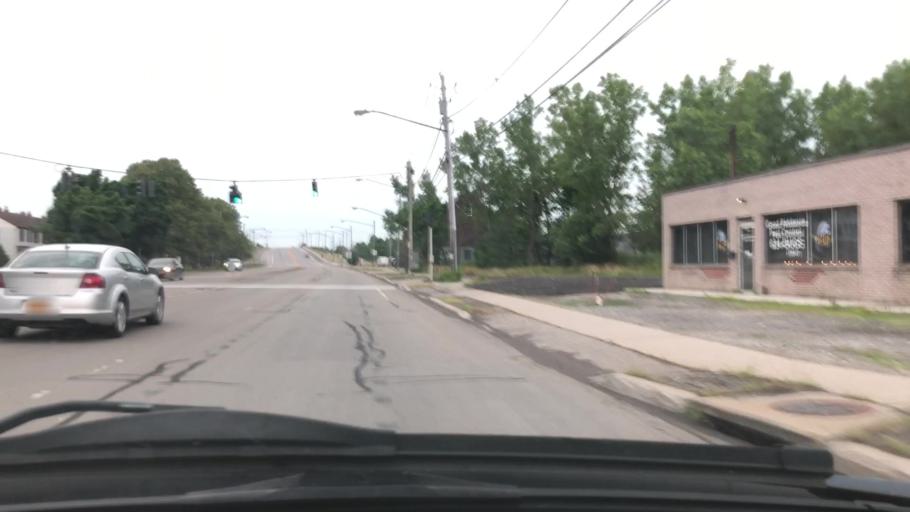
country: US
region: New York
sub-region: Erie County
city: Sloan
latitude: 42.8958
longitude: -78.7843
